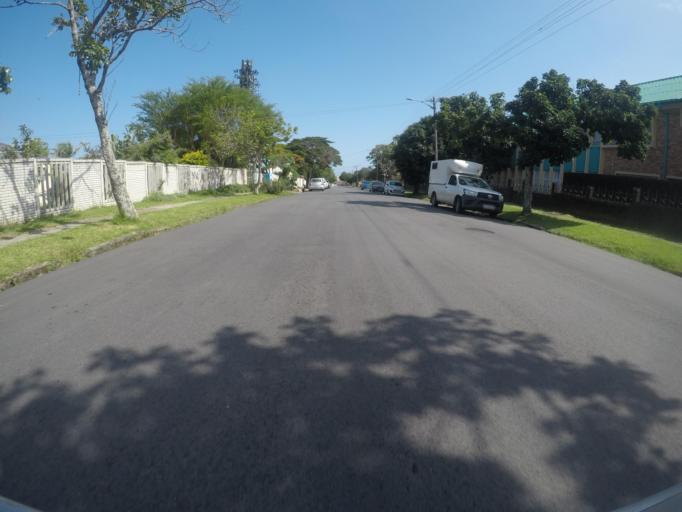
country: ZA
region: Eastern Cape
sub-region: Buffalo City Metropolitan Municipality
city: East London
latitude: -32.9765
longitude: 27.8868
